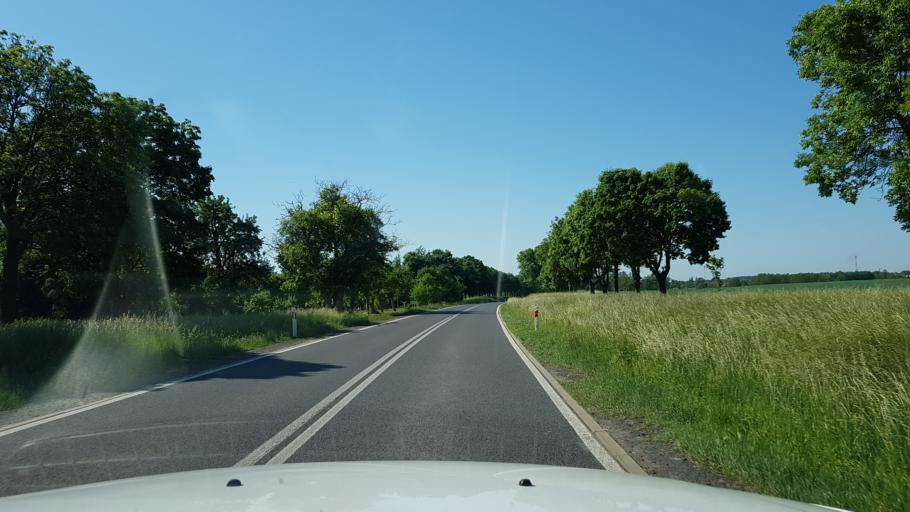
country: PL
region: West Pomeranian Voivodeship
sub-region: Powiat gryfinski
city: Mieszkowice
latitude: 52.8029
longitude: 14.4990
